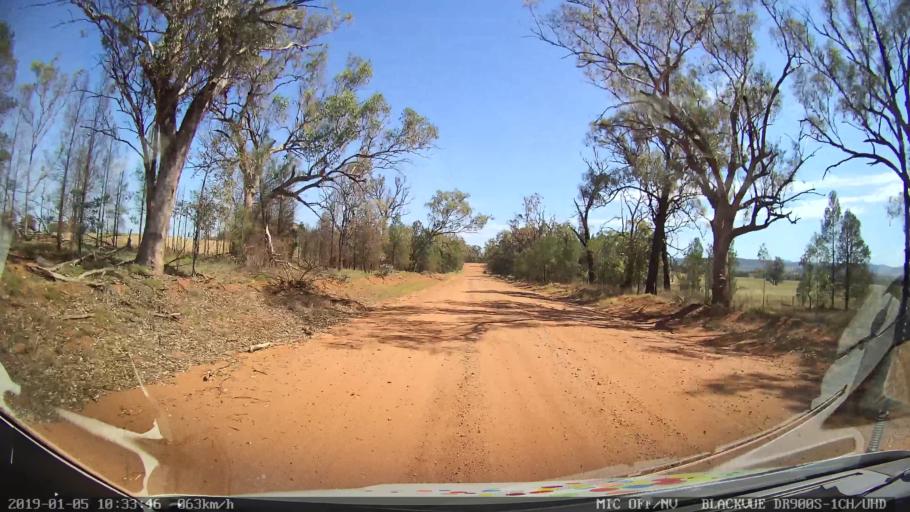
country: AU
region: New South Wales
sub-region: Gilgandra
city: Gilgandra
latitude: -31.5043
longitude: 148.9297
